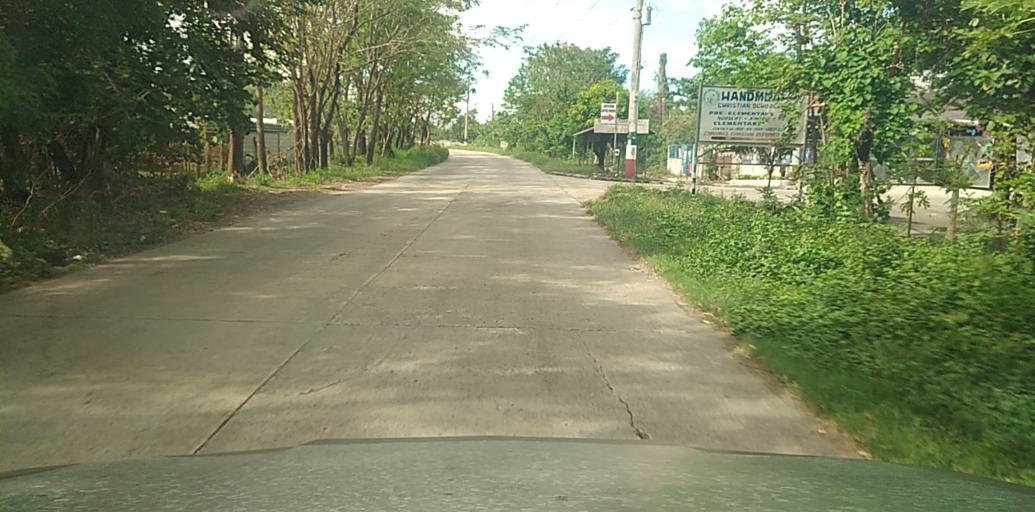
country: PH
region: Central Luzon
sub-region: Province of Pampanga
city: Pandacaqui
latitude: 15.1760
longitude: 120.6672
